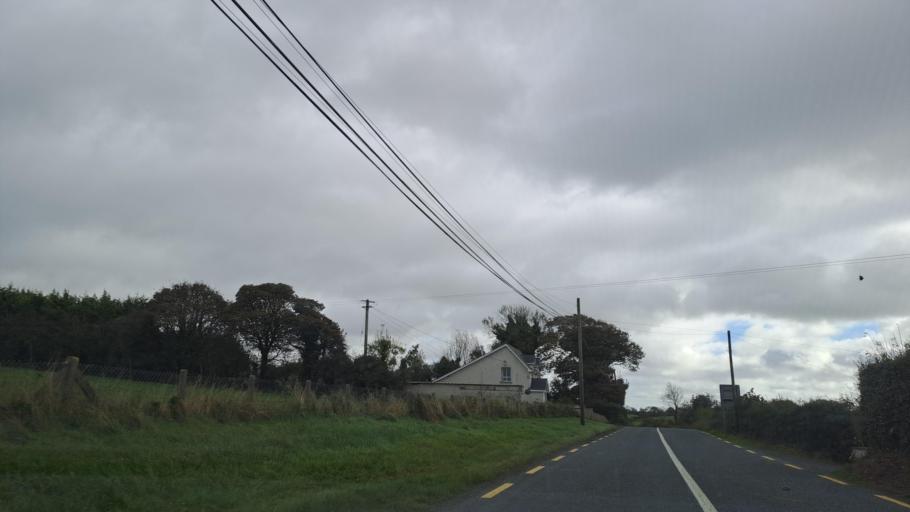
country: IE
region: Ulster
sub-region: An Cabhan
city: Kingscourt
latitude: 53.9113
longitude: -6.8453
